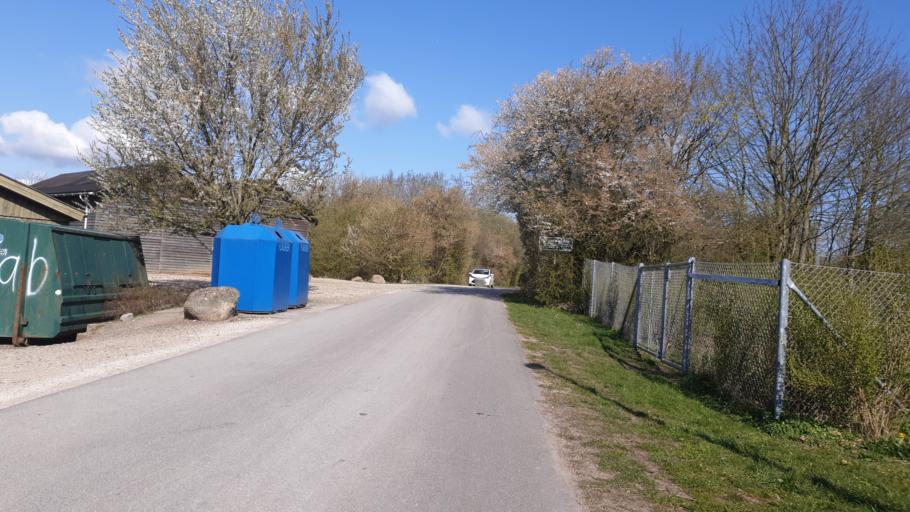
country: DK
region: Central Jutland
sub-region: Hedensted Kommune
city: Hedensted
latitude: 55.8061
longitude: 9.7018
